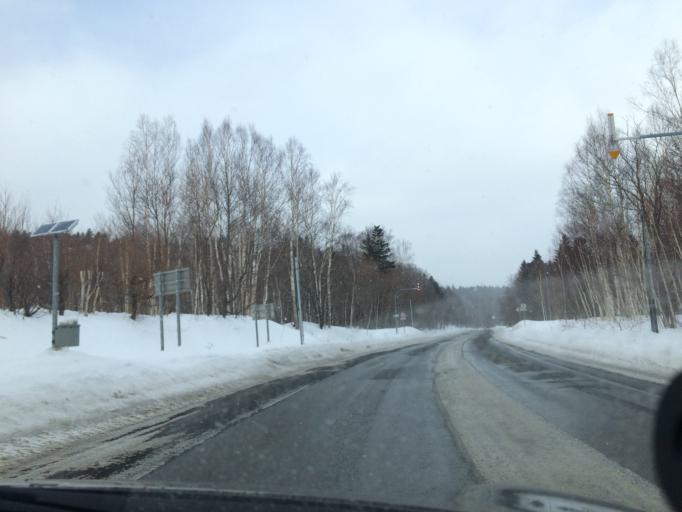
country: JP
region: Hokkaido
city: Shimo-furano
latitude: 43.0544
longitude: 142.6686
